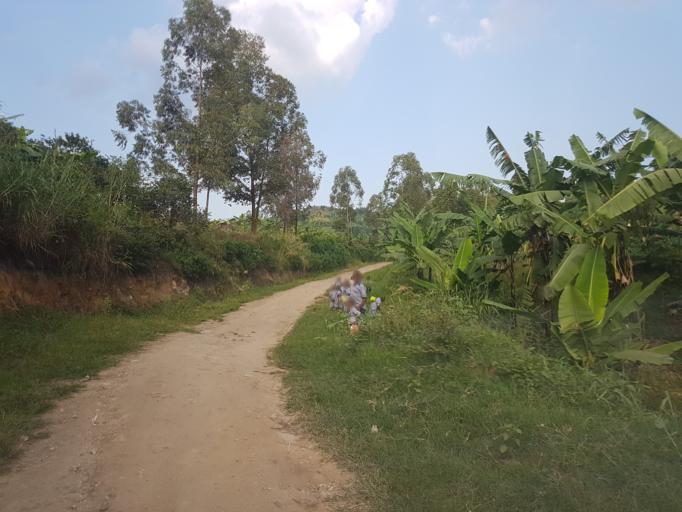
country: UG
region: Western Region
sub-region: Rukungiri District
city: Rukungiri
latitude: -0.6762
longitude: 29.8997
